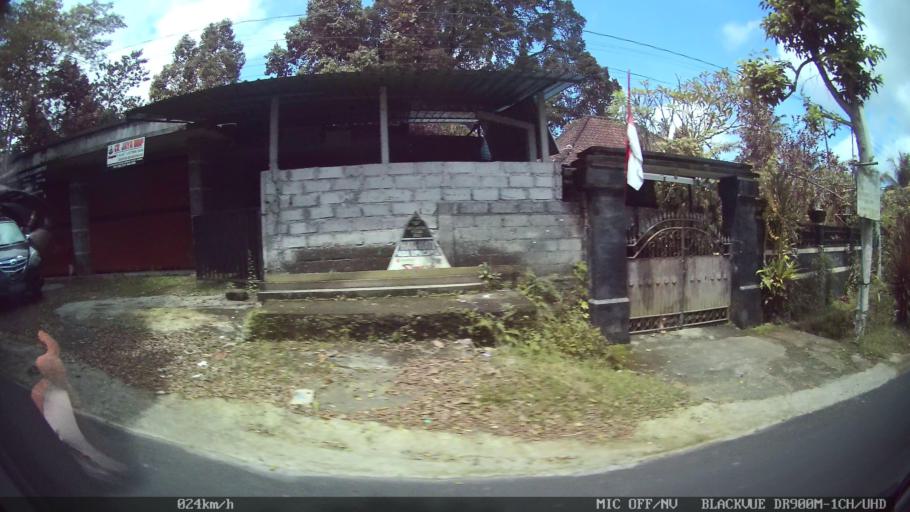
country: ID
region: Bali
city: Banjar Bebalang
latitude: -8.4775
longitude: 115.3420
